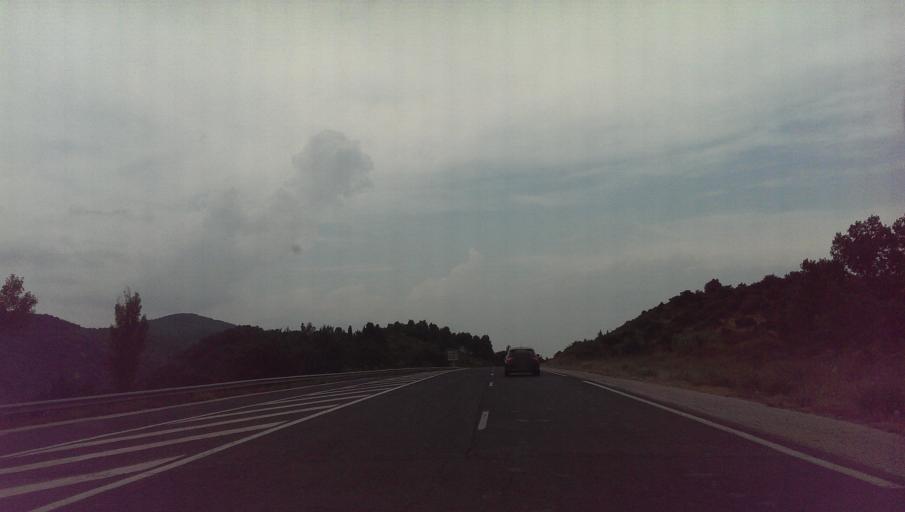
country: FR
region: Languedoc-Roussillon
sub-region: Departement des Pyrenees-Orientales
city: Vinca
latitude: 42.6464
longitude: 2.5147
